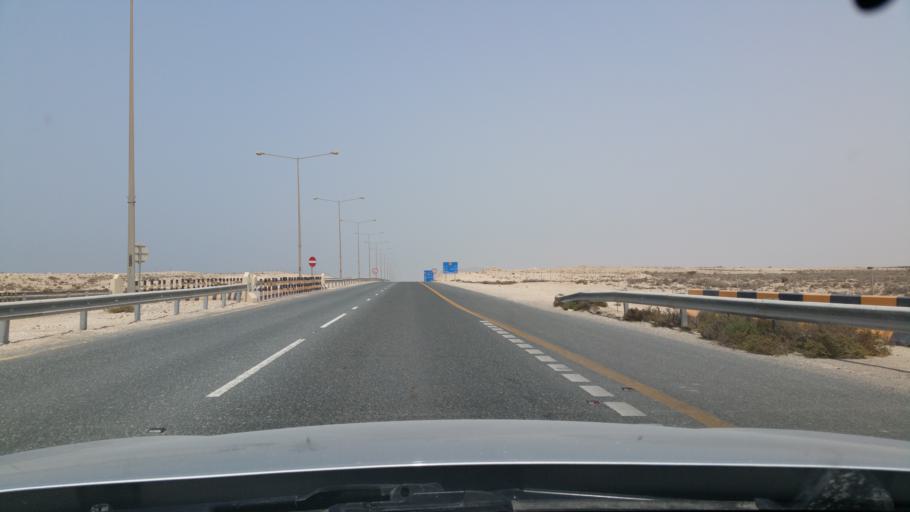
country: QA
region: Baladiyat ar Rayyan
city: Dukhan
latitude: 25.3252
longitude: 50.7874
